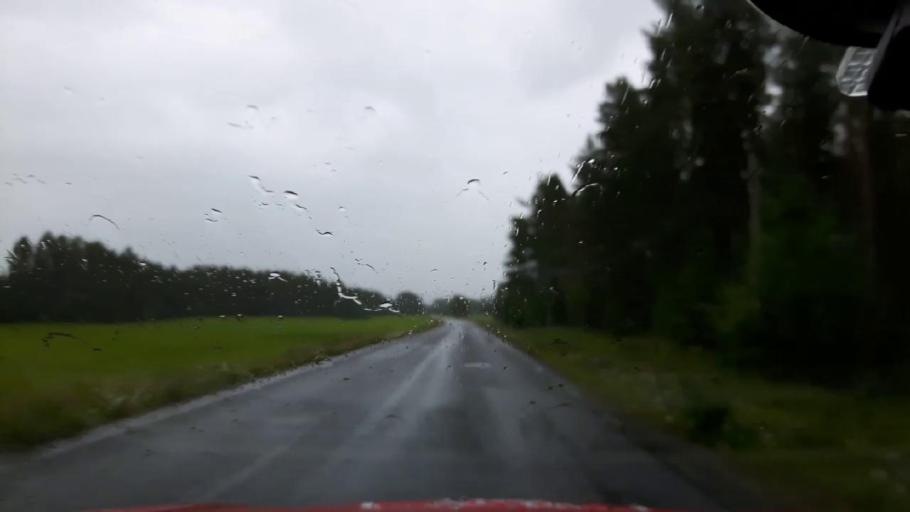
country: SE
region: Jaemtland
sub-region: OEstersunds Kommun
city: Brunflo
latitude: 62.9979
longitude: 14.7651
